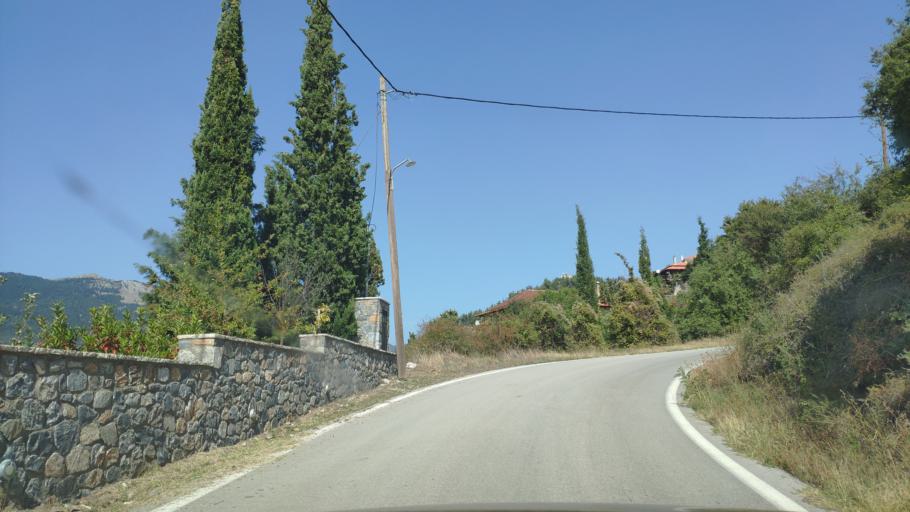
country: GR
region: West Greece
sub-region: Nomos Achaias
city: Aiyira
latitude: 37.9302
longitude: 22.3394
